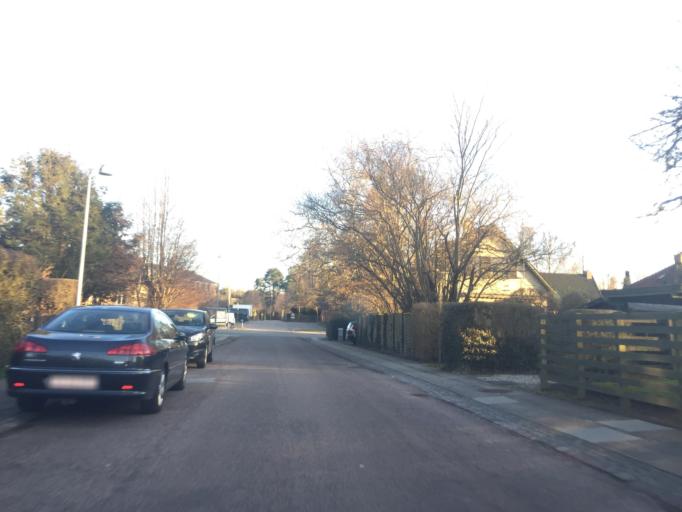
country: DK
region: Capital Region
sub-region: Lyngby-Tarbaek Kommune
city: Kongens Lyngby
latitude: 55.7841
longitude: 12.4887
